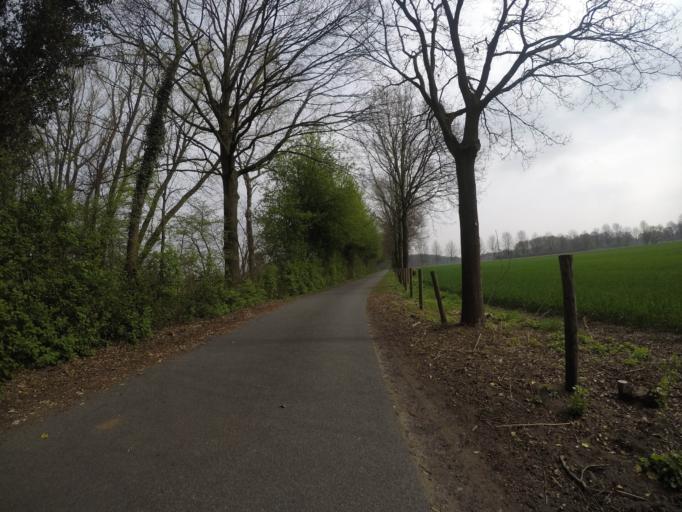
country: DE
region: North Rhine-Westphalia
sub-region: Regierungsbezirk Munster
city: Isselburg
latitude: 51.8651
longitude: 6.5146
